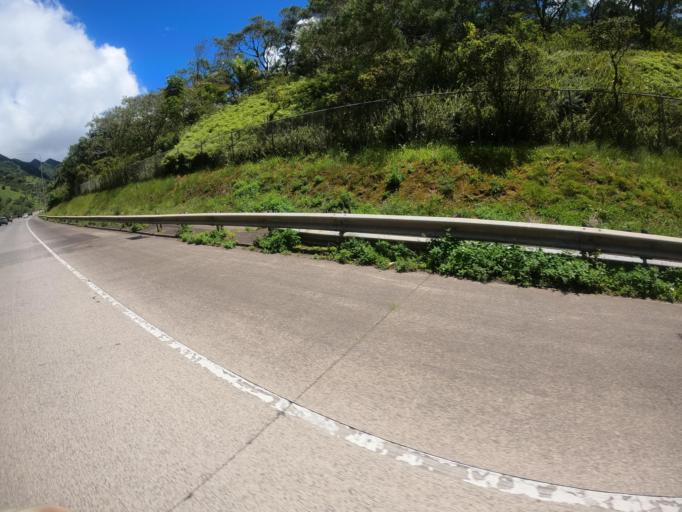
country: US
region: Hawaii
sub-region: Honolulu County
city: Halawa Heights
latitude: 21.4037
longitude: -157.8720
